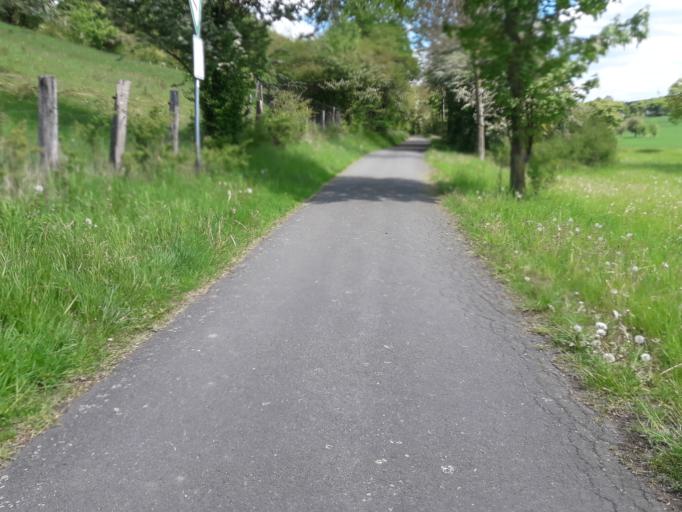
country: DE
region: North Rhine-Westphalia
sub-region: Regierungsbezirk Detmold
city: Paderborn
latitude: 51.6977
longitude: 8.8193
